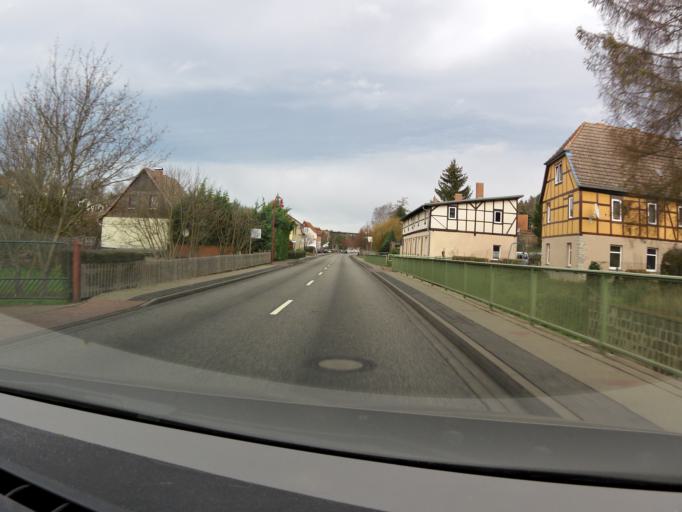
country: DE
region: Saxony-Anhalt
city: Mansfeld
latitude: 51.5961
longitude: 11.4568
